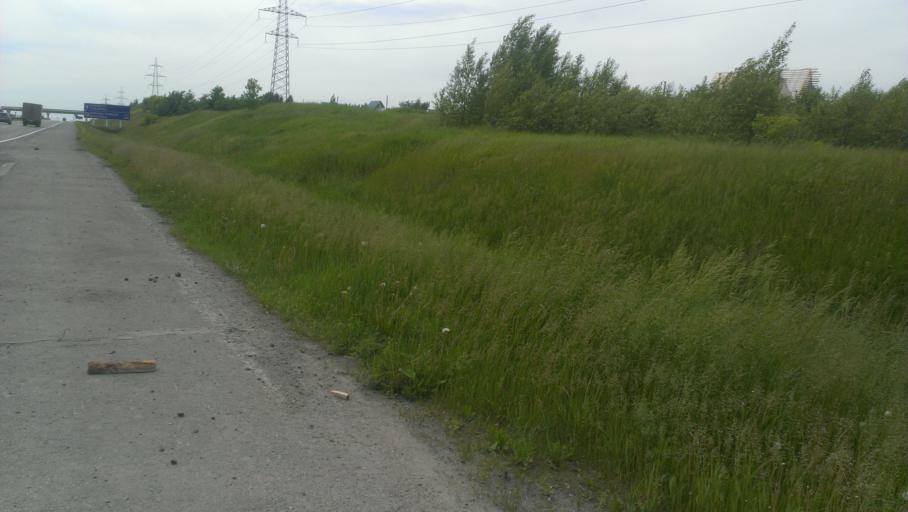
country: RU
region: Altai Krai
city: Sannikovo
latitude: 53.3449
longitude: 83.9422
